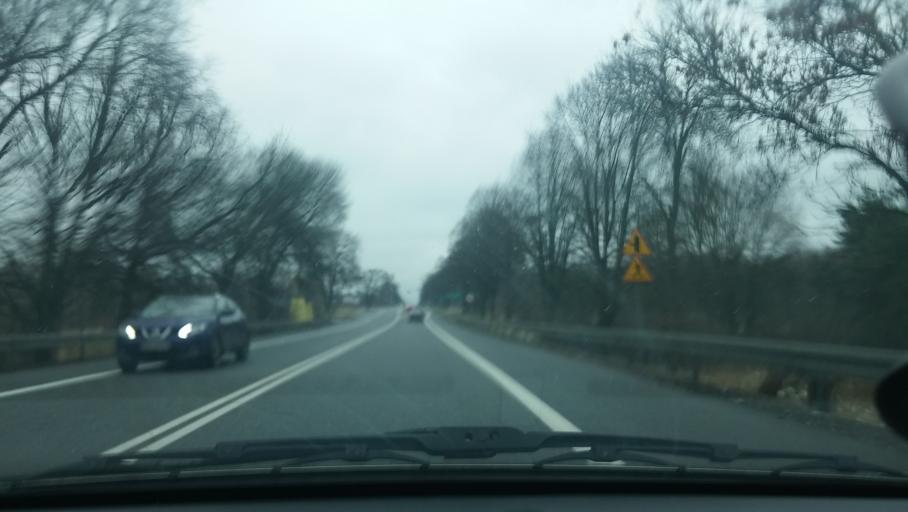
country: PL
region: Masovian Voivodeship
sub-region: Powiat minski
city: Kaluszyn
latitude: 52.2099
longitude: 21.8569
